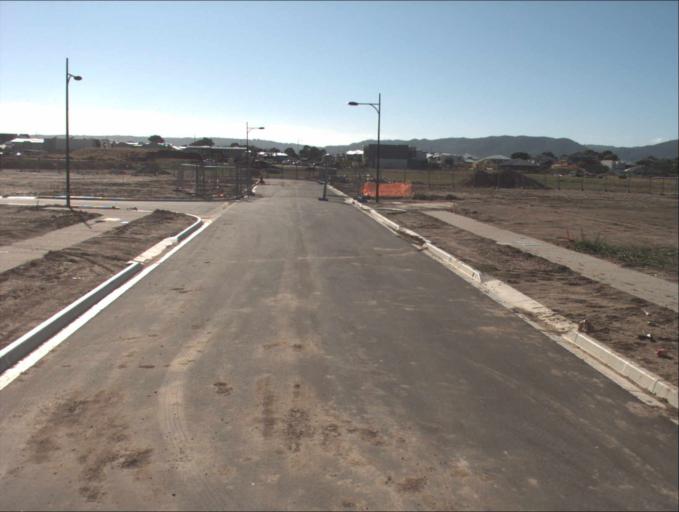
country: AU
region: South Australia
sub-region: Port Adelaide Enfield
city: Klemzig
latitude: -34.8640
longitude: 138.6271
